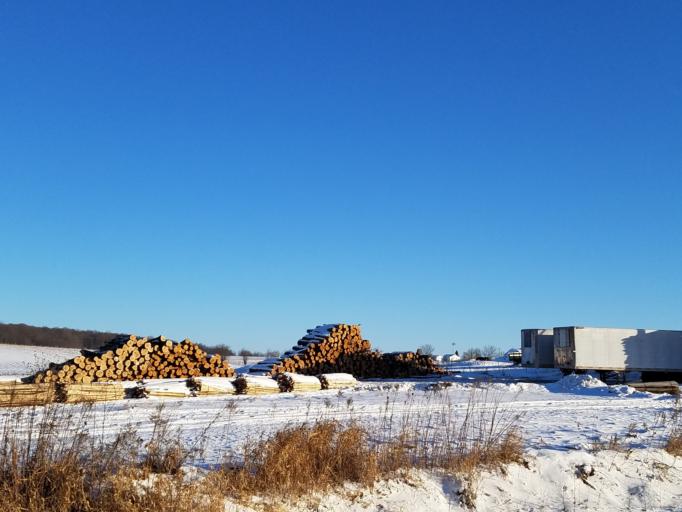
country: US
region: Wisconsin
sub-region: Clark County
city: Loyal
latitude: 44.5964
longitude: -90.4429
